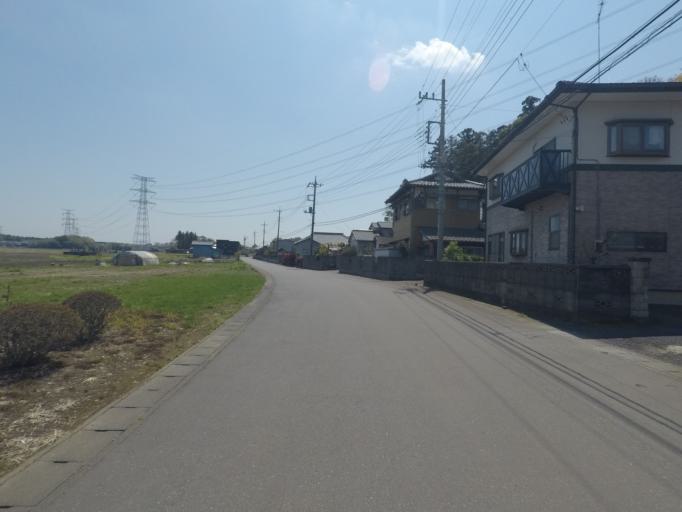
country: JP
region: Ibaraki
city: Ushiku
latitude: 36.0142
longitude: 140.0922
